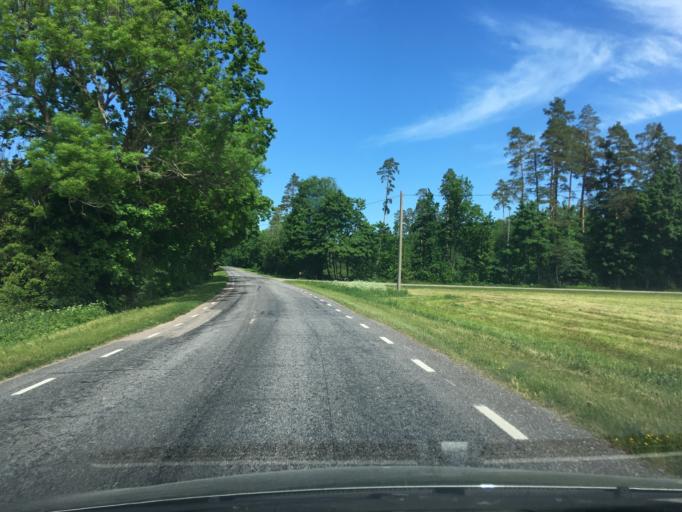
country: EE
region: Raplamaa
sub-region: Rapla vald
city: Rapla
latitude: 59.0590
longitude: 24.9102
